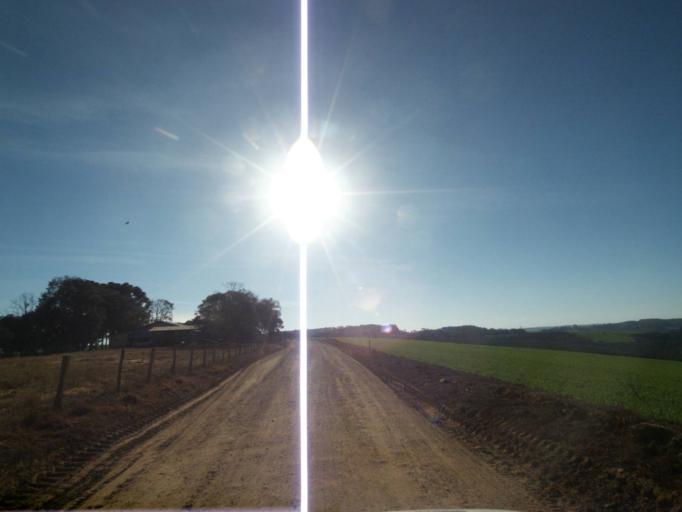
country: BR
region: Parana
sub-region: Telemaco Borba
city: Telemaco Borba
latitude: -24.5222
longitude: -50.6415
